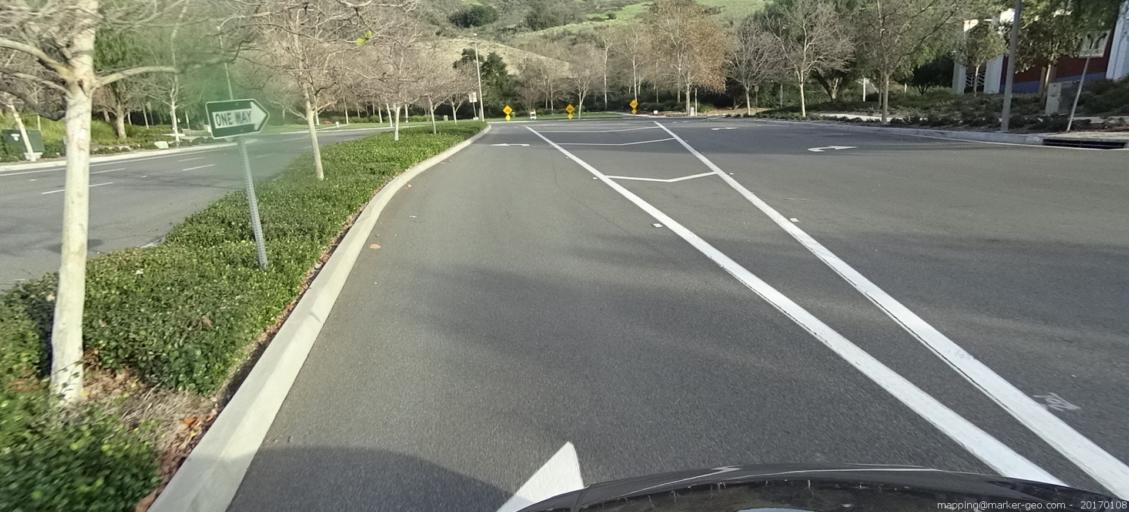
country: US
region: California
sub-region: Orange County
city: Ladera Ranch
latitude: 33.5652
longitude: -117.6279
